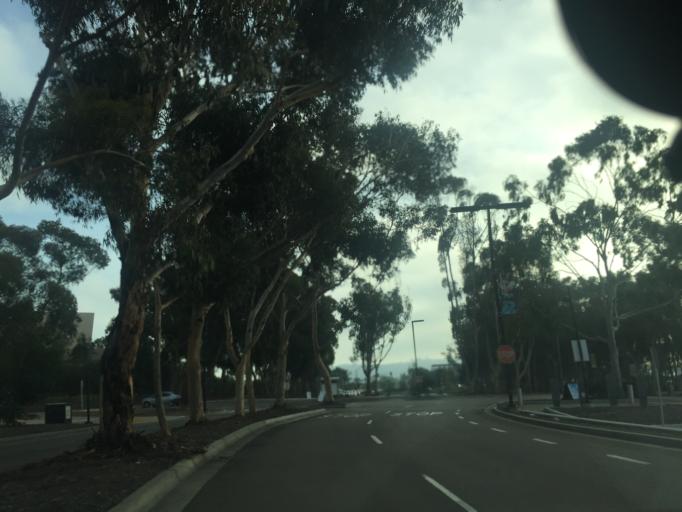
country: US
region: California
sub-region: San Diego County
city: La Jolla
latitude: 32.8723
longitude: -117.2419
